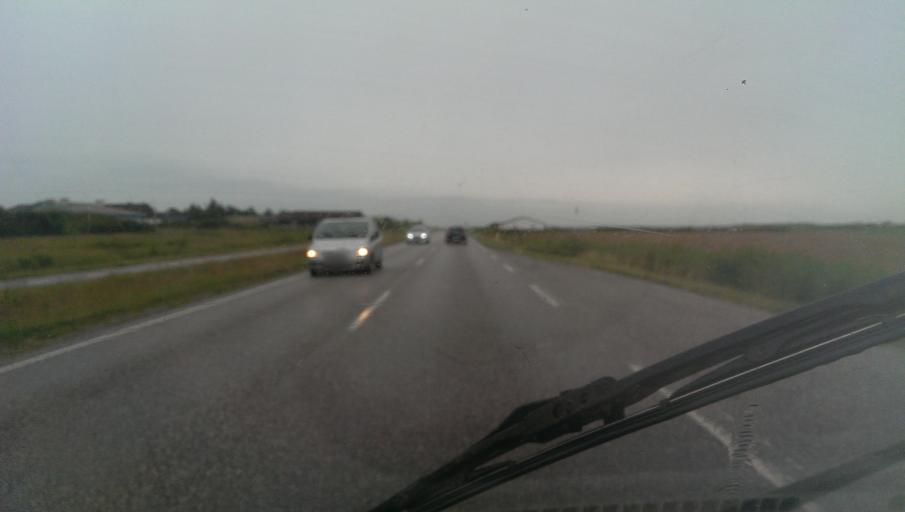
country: DK
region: Central Jutland
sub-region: Ringkobing-Skjern Kommune
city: Ringkobing
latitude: 56.1429
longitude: 8.1248
